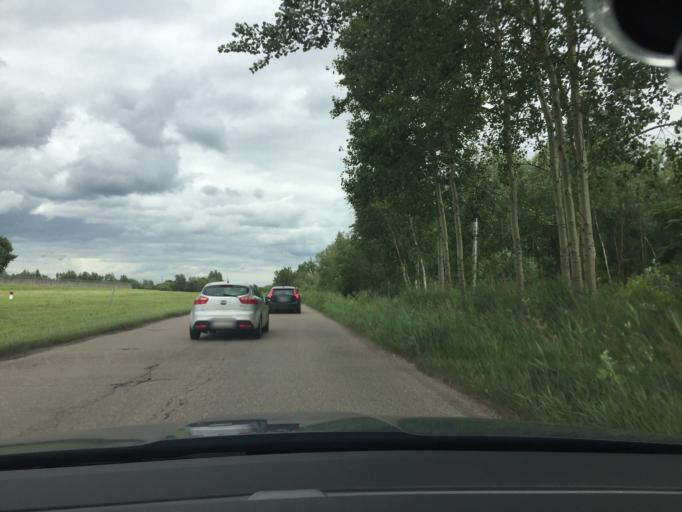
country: PL
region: Pomeranian Voivodeship
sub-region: Gdansk
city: Gdansk
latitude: 54.3535
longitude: 18.7494
